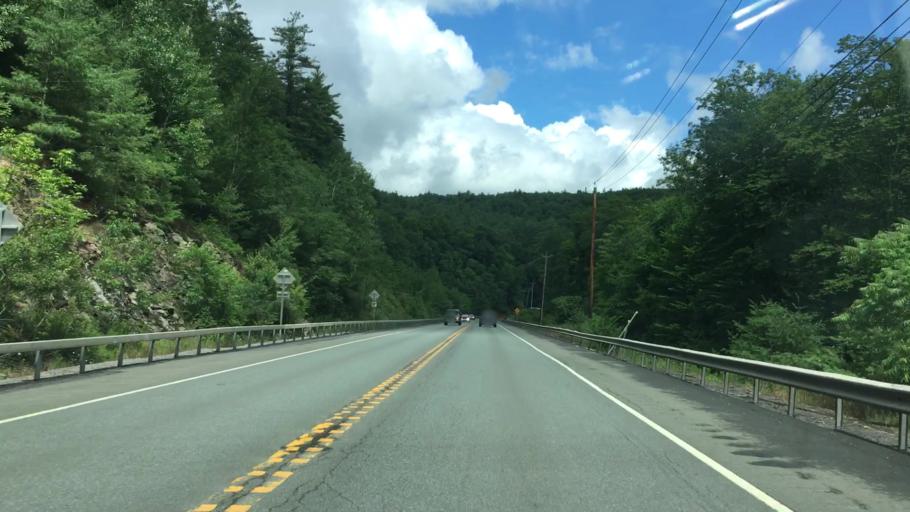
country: US
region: New York
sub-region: Rensselaer County
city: Hoosick Falls
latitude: 42.8430
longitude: -73.3682
